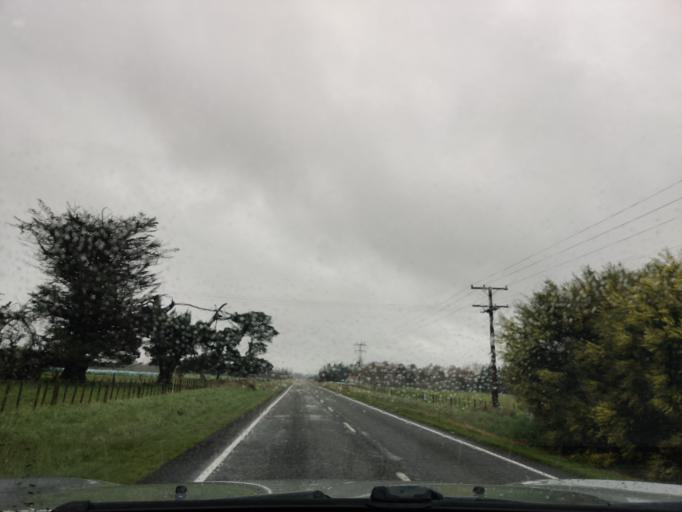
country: NZ
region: Hawke's Bay
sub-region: Hastings District
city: Hastings
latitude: -40.0184
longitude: 176.3470
